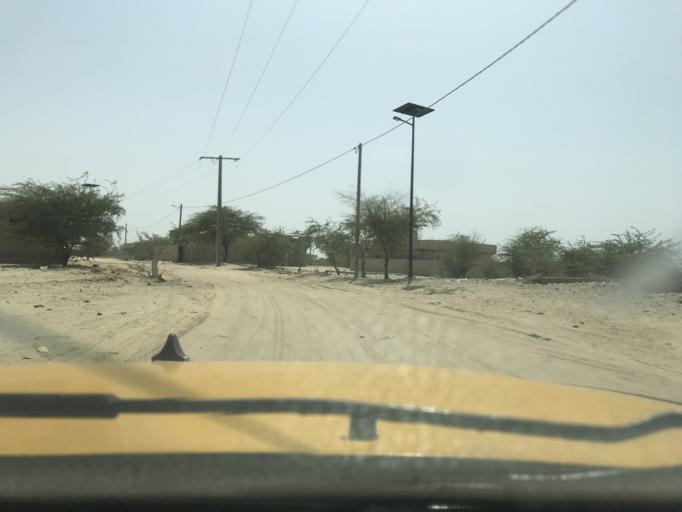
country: SN
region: Saint-Louis
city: Saint-Louis
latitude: 16.0184
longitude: -16.4471
